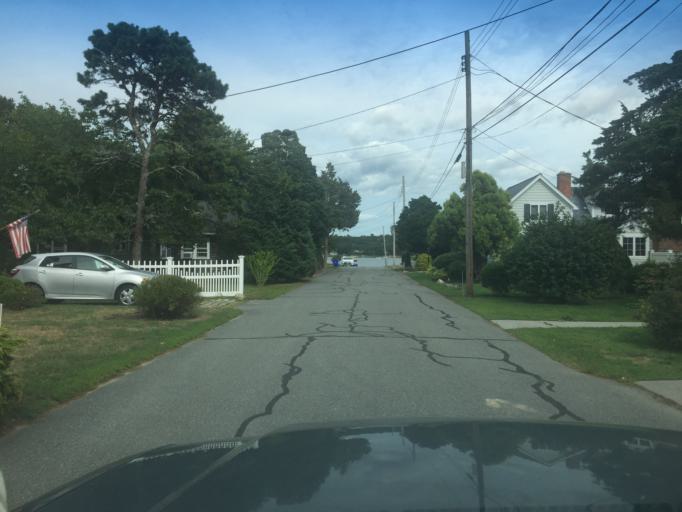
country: US
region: Massachusetts
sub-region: Barnstable County
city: Pocasset
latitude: 41.6823
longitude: -70.6265
